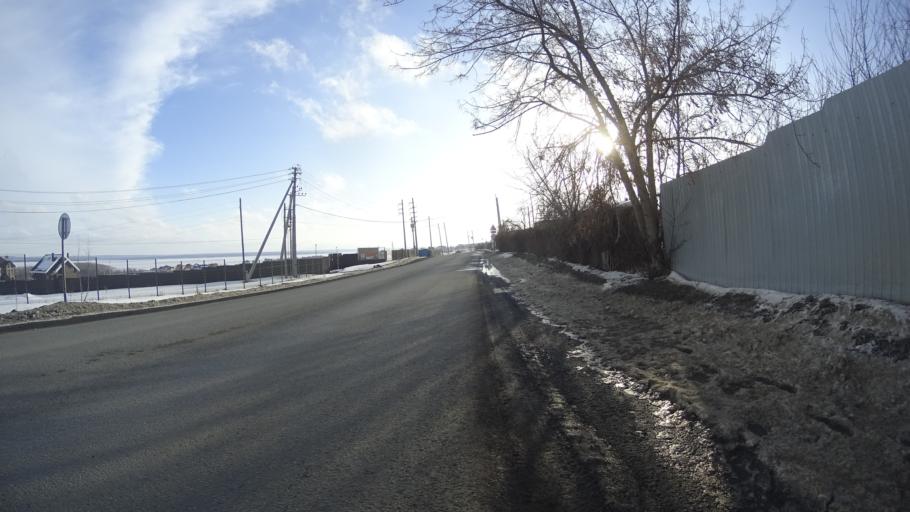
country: RU
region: Chelyabinsk
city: Sargazy
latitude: 55.1245
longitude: 61.2892
